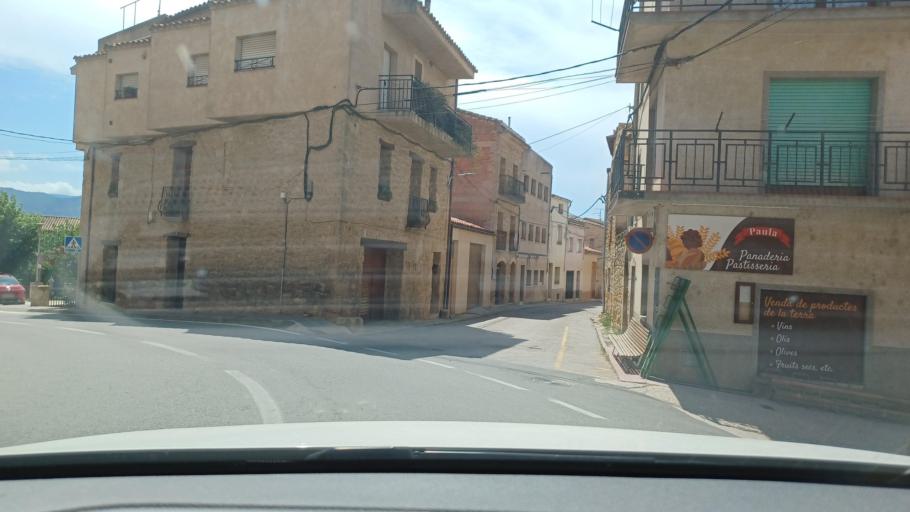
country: ES
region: Catalonia
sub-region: Provincia de Tarragona
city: Horta de Sant Joan
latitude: 40.9553
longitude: 0.3147
